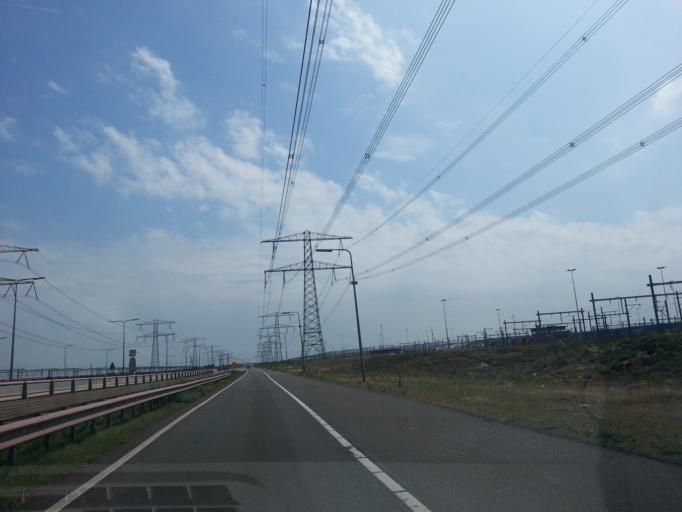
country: NL
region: South Holland
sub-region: Gemeente Rotterdam
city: Hoek van Holland
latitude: 51.9446
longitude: 4.0261
